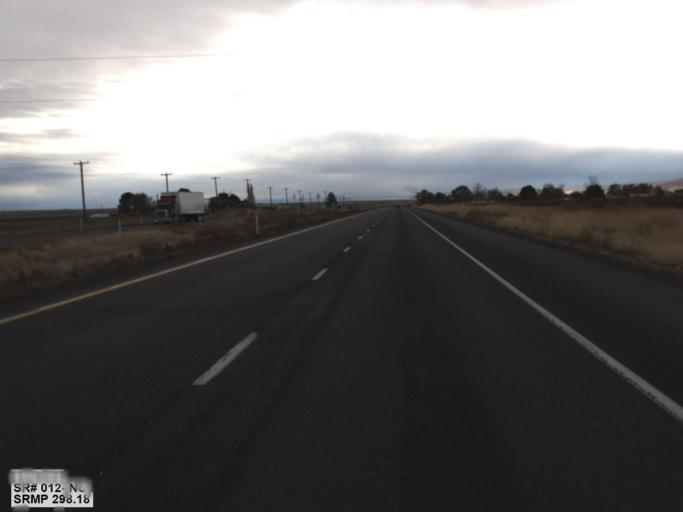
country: US
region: Washington
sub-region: Walla Walla County
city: Burbank
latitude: 46.1799
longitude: -118.9710
